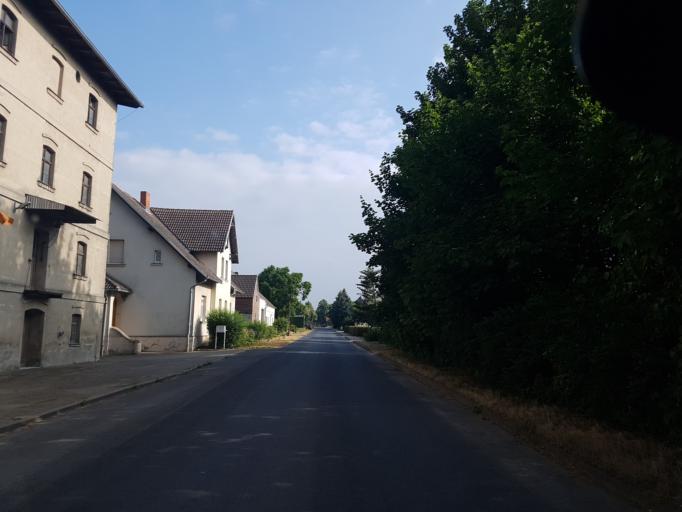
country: DE
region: Saxony-Anhalt
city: Kropstadt
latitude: 52.0074
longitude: 12.8191
